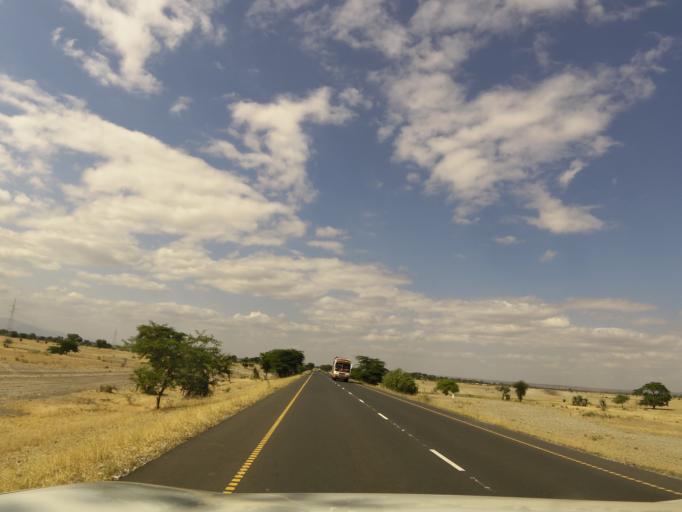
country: TZ
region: Arusha
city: Mto wa Mbu
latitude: -3.6695
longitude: 35.9525
